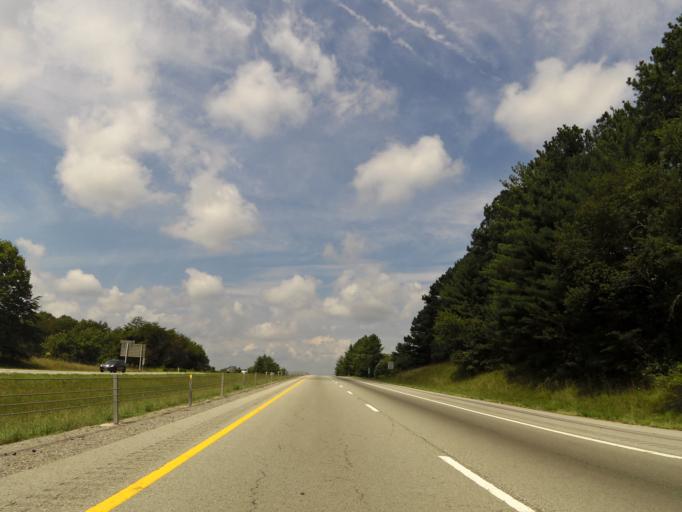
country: US
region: Tennessee
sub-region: Cumberland County
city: Fairfield Glade
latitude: 35.9135
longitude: -84.8963
